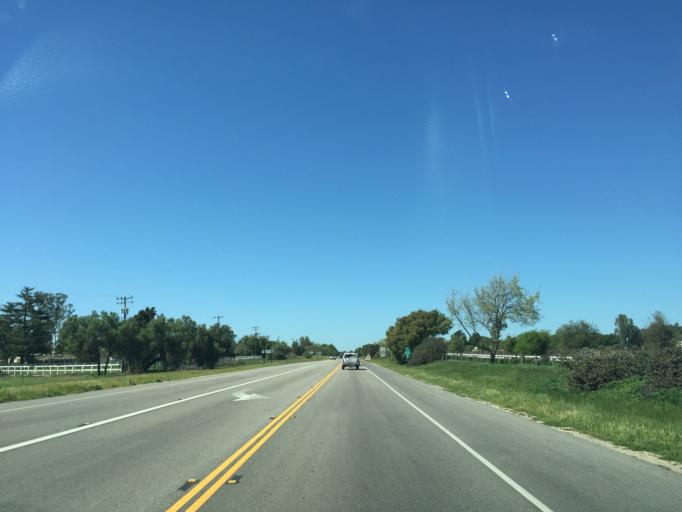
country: US
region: California
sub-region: Santa Barbara County
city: Los Olivos
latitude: 34.6510
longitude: -120.0957
